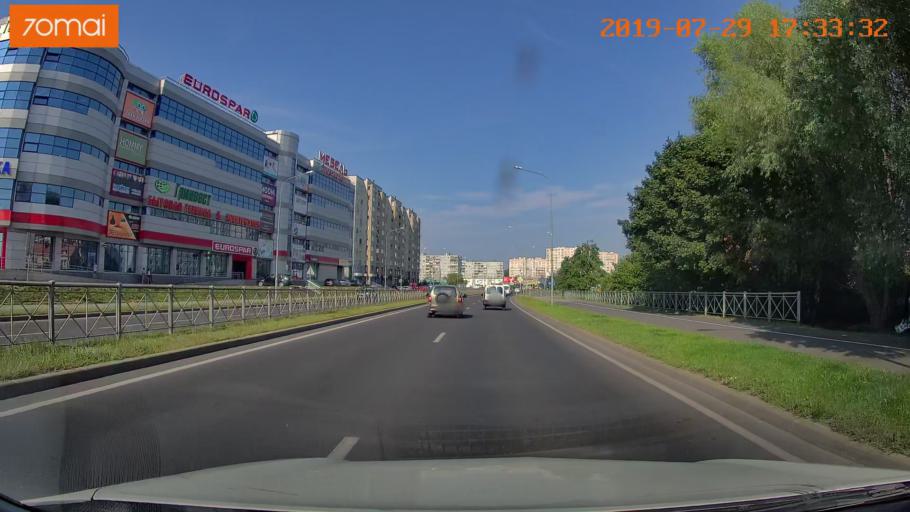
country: RU
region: Kaliningrad
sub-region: Gorod Kaliningrad
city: Kaliningrad
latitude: 54.7414
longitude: 20.4992
